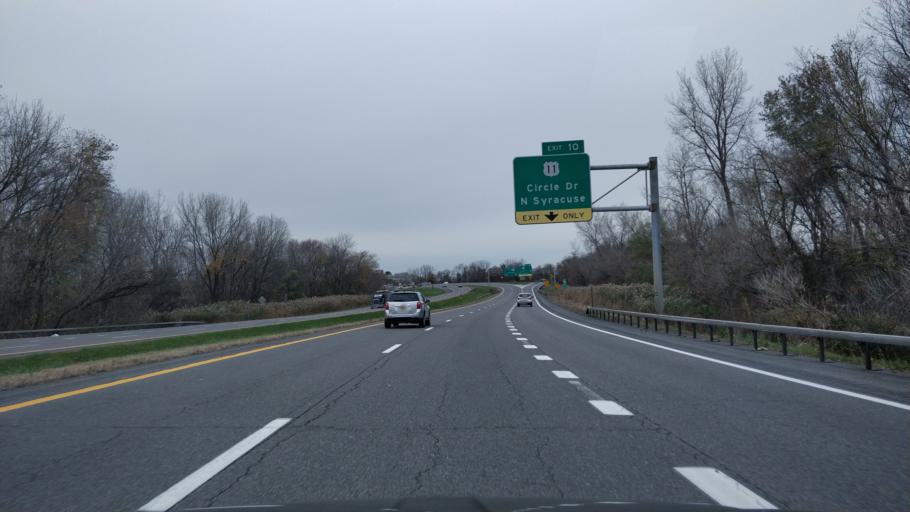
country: US
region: New York
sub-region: Onondaga County
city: North Syracuse
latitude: 43.1438
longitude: -76.1203
